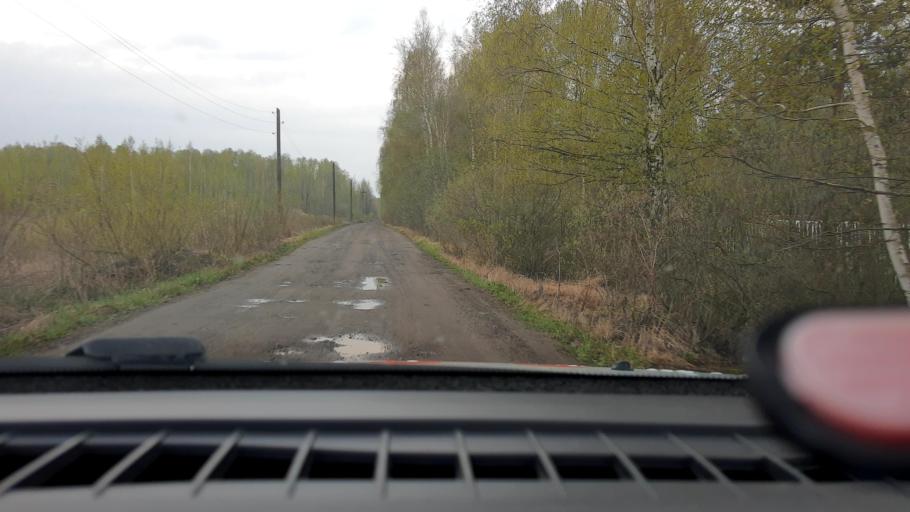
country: RU
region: Nizjnij Novgorod
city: Gorbatovka
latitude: 56.3038
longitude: 43.7696
